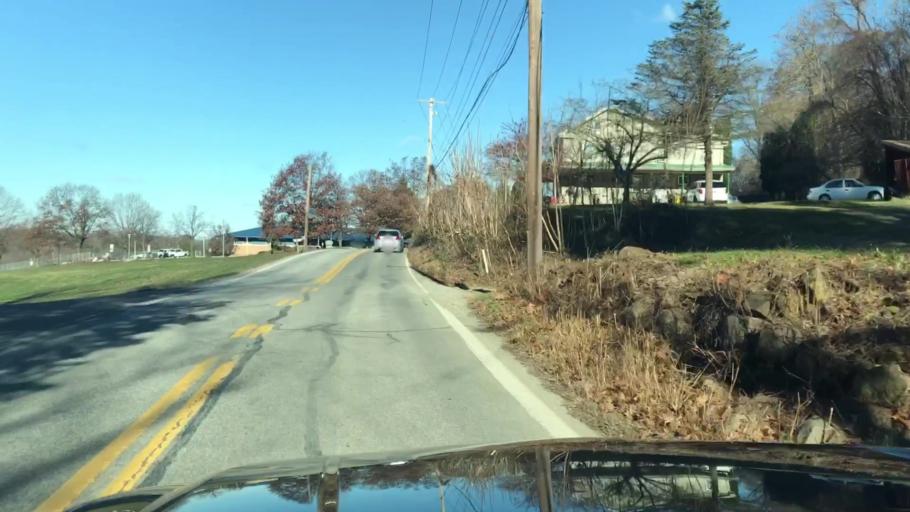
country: US
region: Pennsylvania
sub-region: Cumberland County
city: Lower Allen
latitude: 40.1883
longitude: -76.8894
